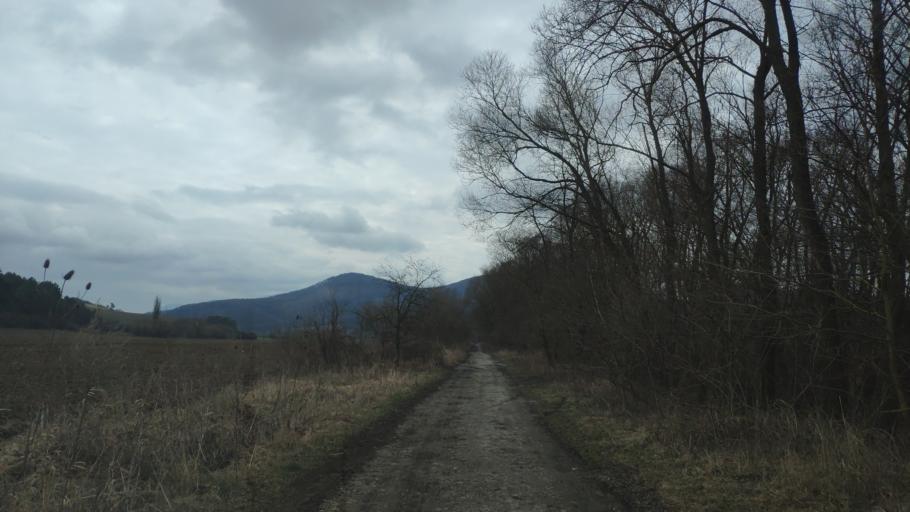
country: SK
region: Presovsky
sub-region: Okres Presov
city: Presov
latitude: 49.0859
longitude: 21.2835
